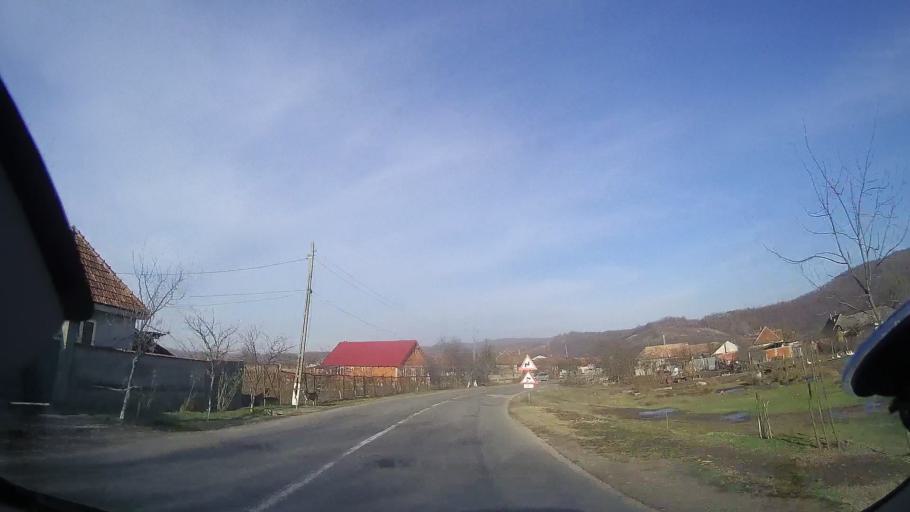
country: RO
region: Bihor
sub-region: Comuna Brusturi
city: Brusturi
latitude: 47.1360
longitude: 22.2684
